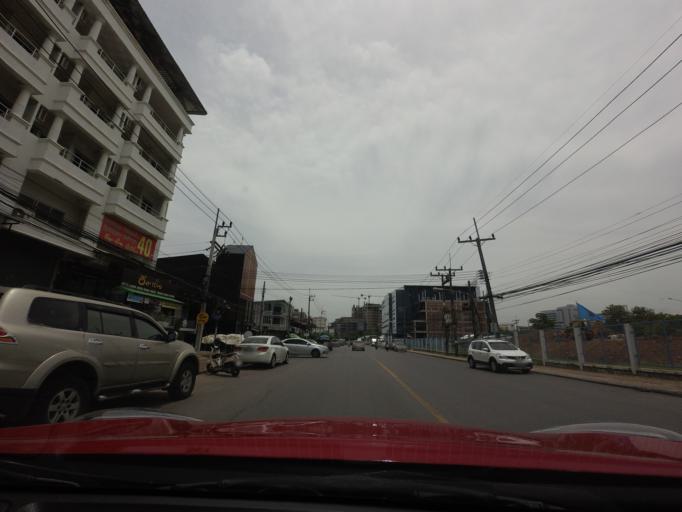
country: TH
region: Songkhla
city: Hat Yai
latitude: 7.0012
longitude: 100.5024
